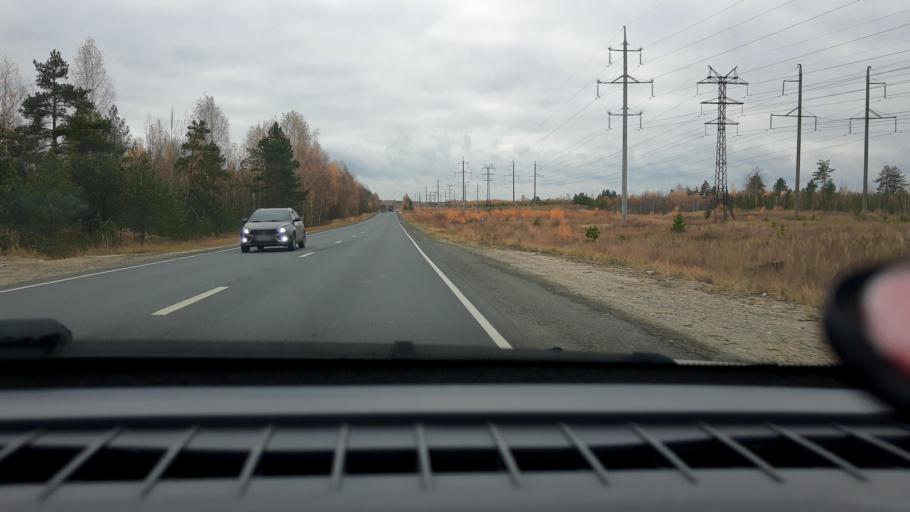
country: RU
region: Nizjnij Novgorod
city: Lukino
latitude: 56.3783
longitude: 43.6279
